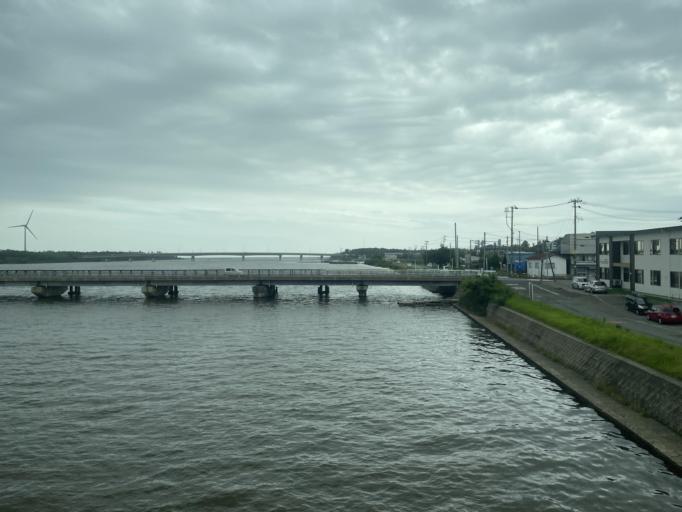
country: JP
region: Akita
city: Tenno
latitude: 39.9029
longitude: 139.9563
